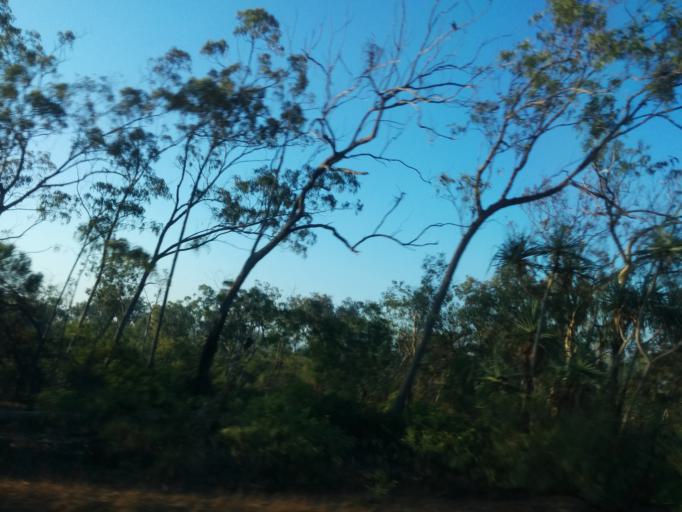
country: AU
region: Northern Territory
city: Alyangula
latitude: -13.8724
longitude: 136.7841
